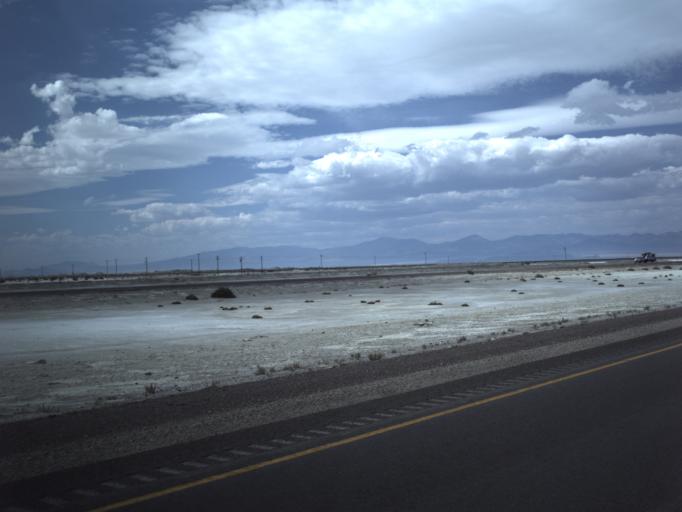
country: US
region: Utah
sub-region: Tooele County
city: Wendover
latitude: 40.7387
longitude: -113.8159
